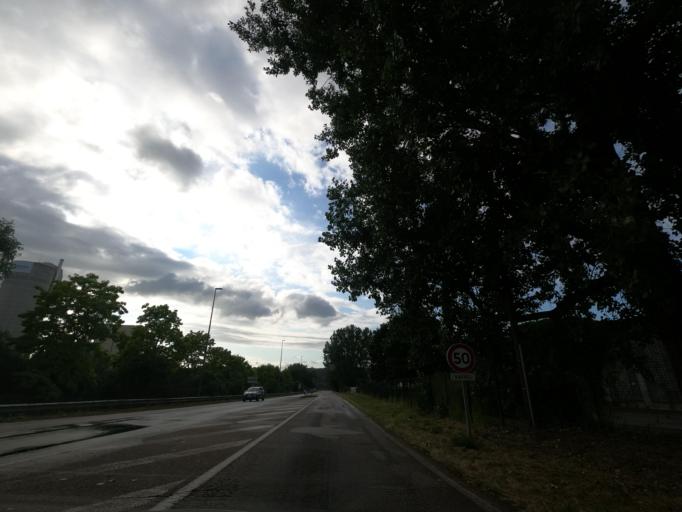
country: FR
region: Haute-Normandie
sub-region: Departement de la Seine-Maritime
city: Grand-Couronne
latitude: 49.3677
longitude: 1.0095
